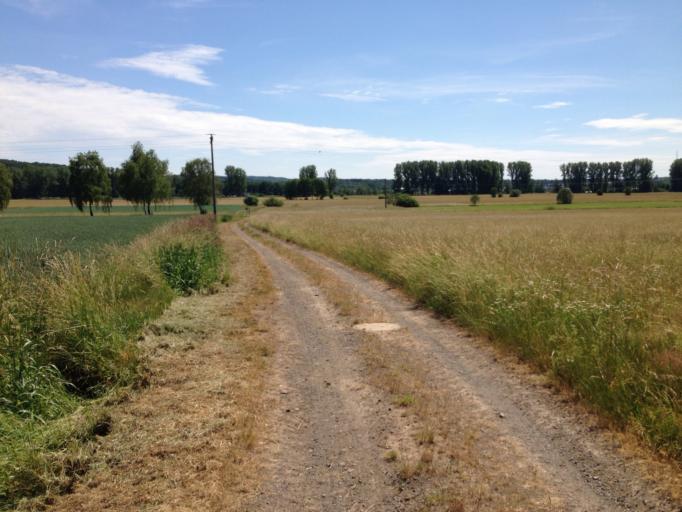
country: DE
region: Hesse
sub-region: Regierungsbezirk Giessen
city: Alten Buseck
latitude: 50.6124
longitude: 8.7354
